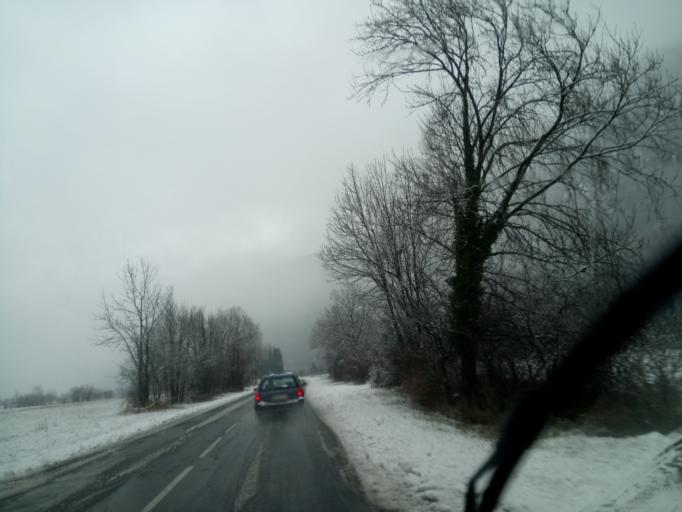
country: FR
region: Rhone-Alpes
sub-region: Departement de la Savoie
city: Saint-Etienne-de-Cuines
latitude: 45.3742
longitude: 6.2757
